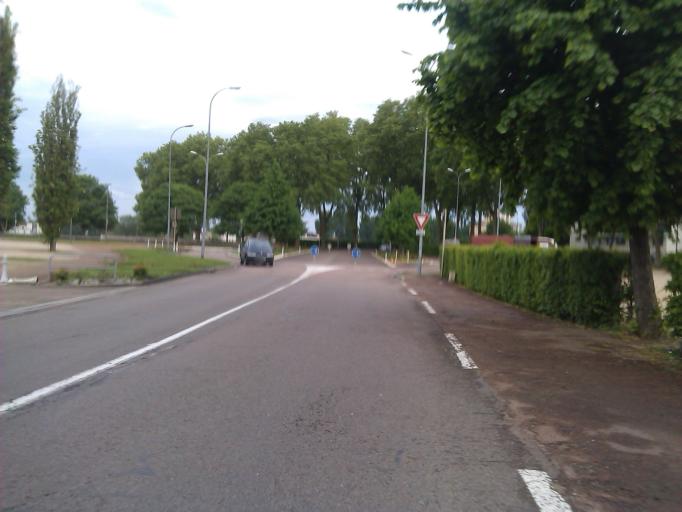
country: FR
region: Bourgogne
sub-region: Departement de Saone-et-Loire
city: Chalon-sur-Saone
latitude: 46.7850
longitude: 4.8634
